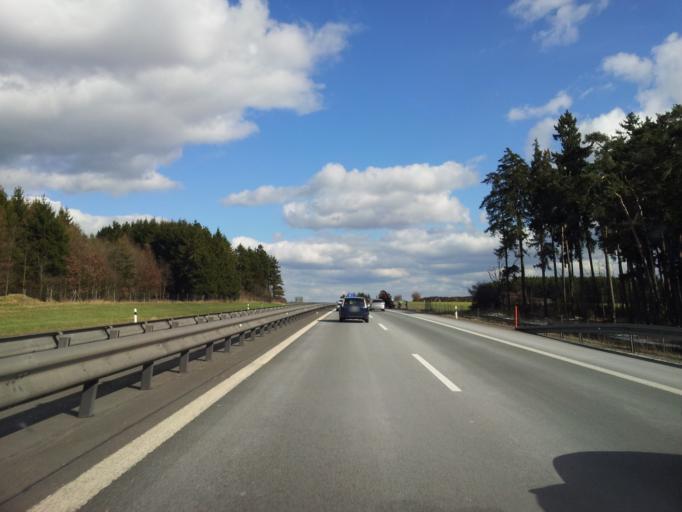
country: DE
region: Bavaria
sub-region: Upper Franconia
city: Feilitzsch
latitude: 50.3764
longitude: 11.9232
